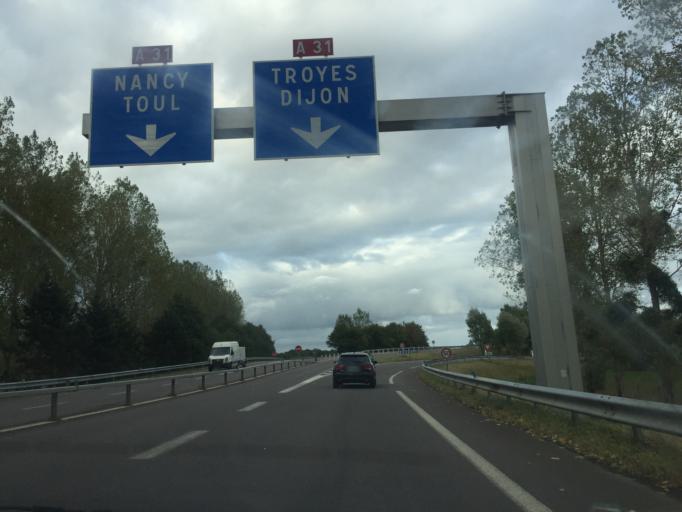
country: FR
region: Lorraine
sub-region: Departement des Vosges
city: Chatenois
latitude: 48.3003
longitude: 5.8548
